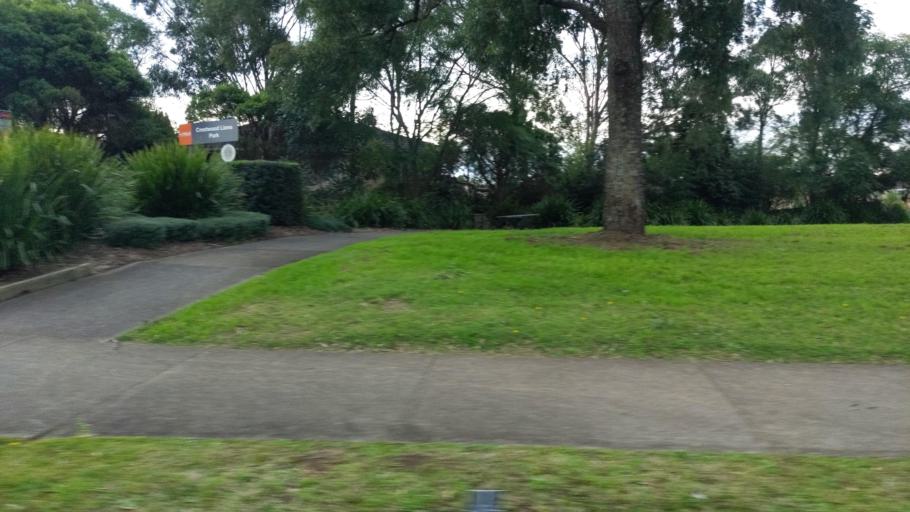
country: AU
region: New South Wales
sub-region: The Hills Shire
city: Baulkham Hills
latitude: -33.7538
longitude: 150.9591
